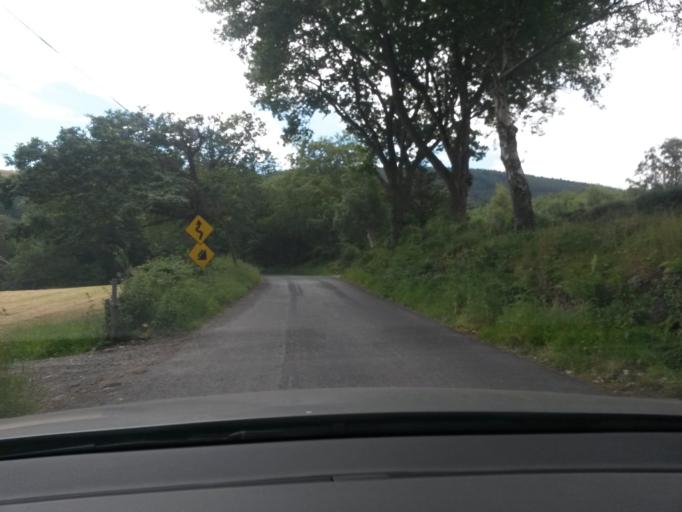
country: IE
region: Leinster
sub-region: Wicklow
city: Enniskerry
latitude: 53.1584
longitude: -6.1999
